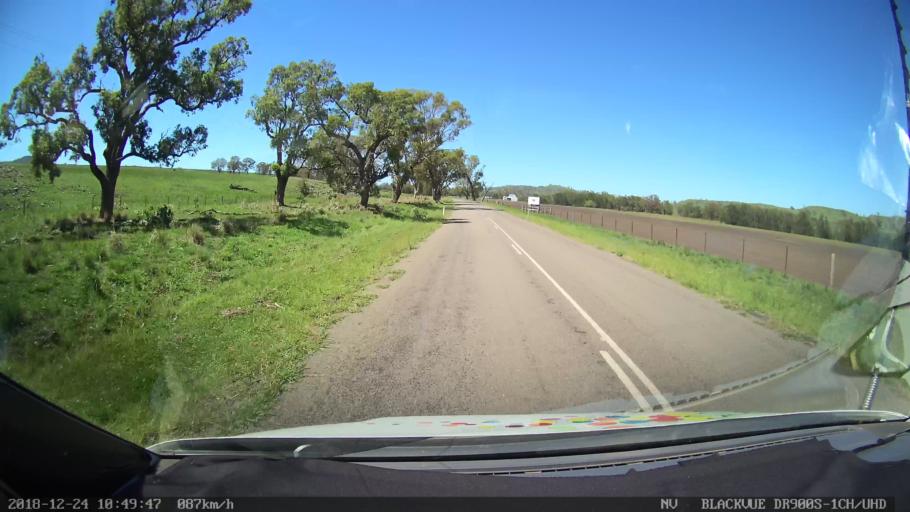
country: AU
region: New South Wales
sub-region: Upper Hunter Shire
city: Merriwa
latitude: -31.9517
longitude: 150.4259
